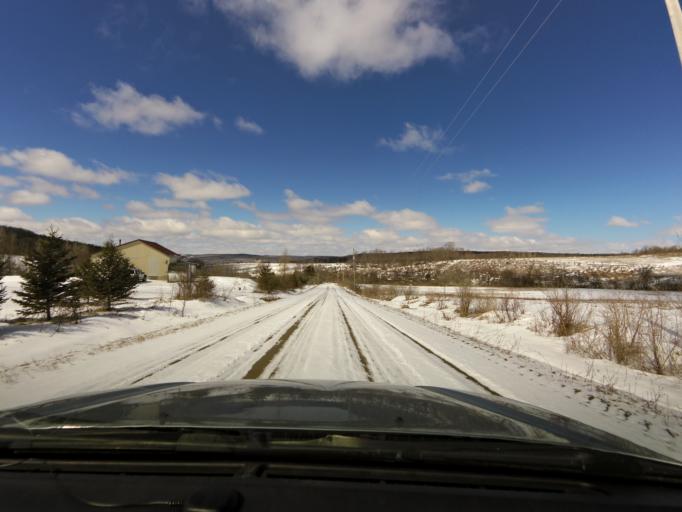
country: US
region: New York
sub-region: Cattaraugus County
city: Franklinville
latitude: 42.3435
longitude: -78.4110
